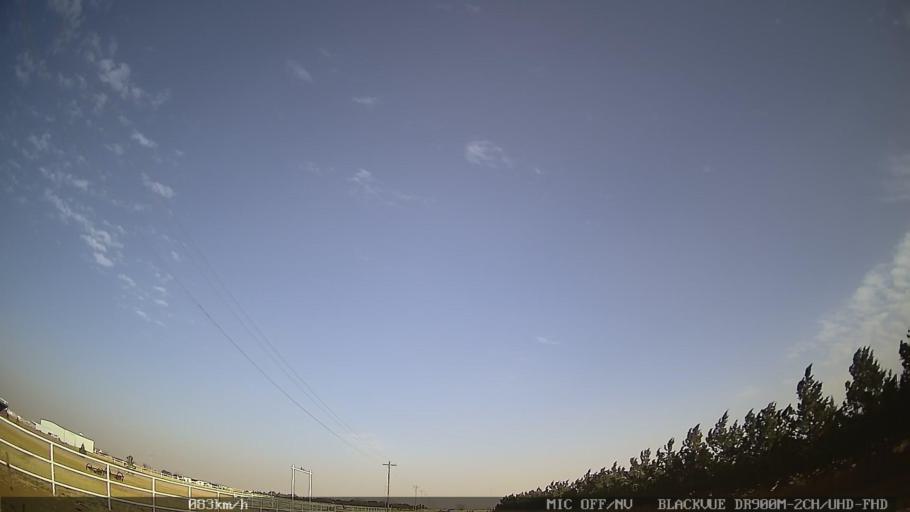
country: US
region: New Mexico
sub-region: Curry County
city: Texico
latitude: 34.4191
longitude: -103.0963
